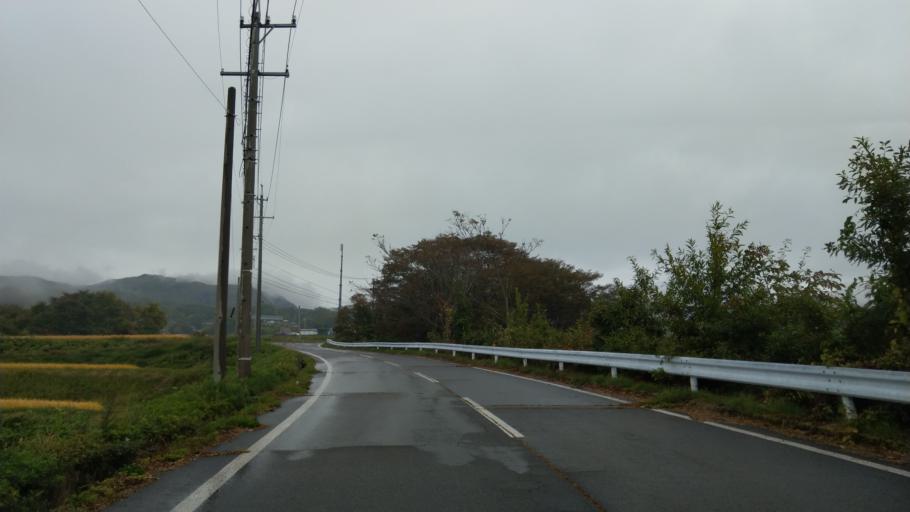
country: JP
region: Nagano
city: Komoro
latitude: 36.3529
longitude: 138.4227
